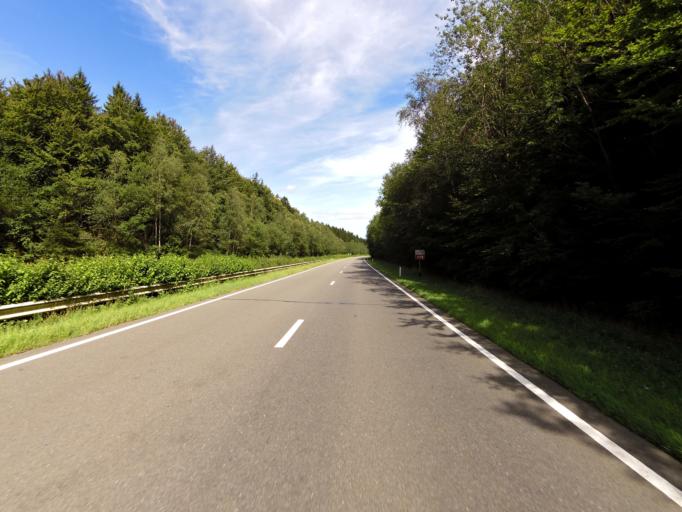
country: BE
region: Wallonia
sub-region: Province du Luxembourg
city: Tenneville
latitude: 50.0987
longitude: 5.4616
